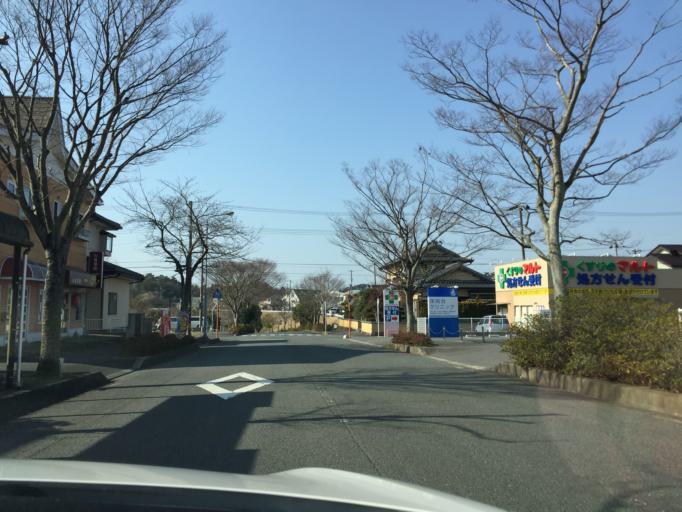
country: JP
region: Fukushima
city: Iwaki
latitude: 36.9648
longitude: 140.9344
